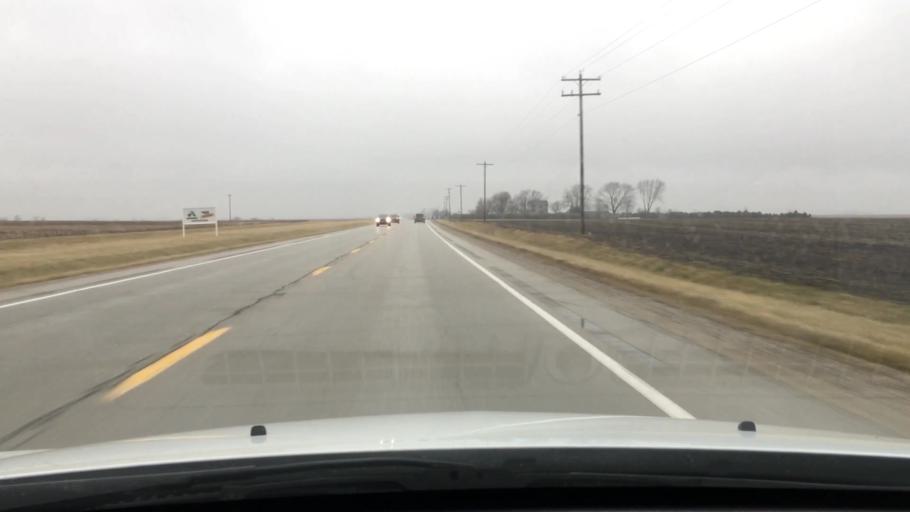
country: US
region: Illinois
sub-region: Livingston County
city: Flanagan
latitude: 40.8718
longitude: -88.8118
